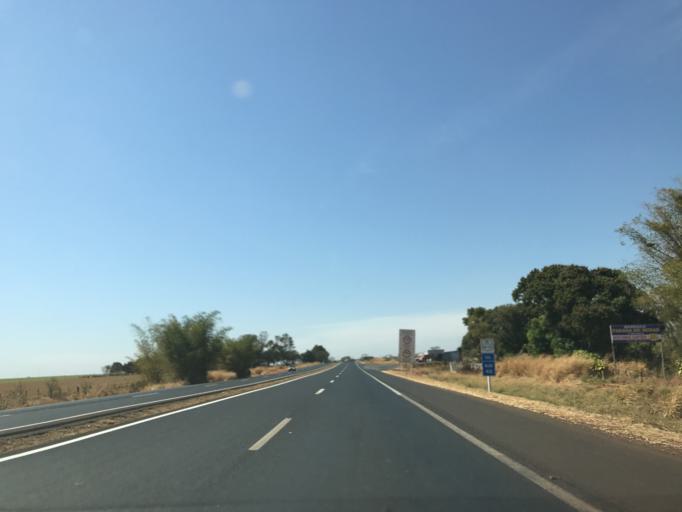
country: BR
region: Minas Gerais
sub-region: Centralina
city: Centralina
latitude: -18.7424
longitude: -49.0949
